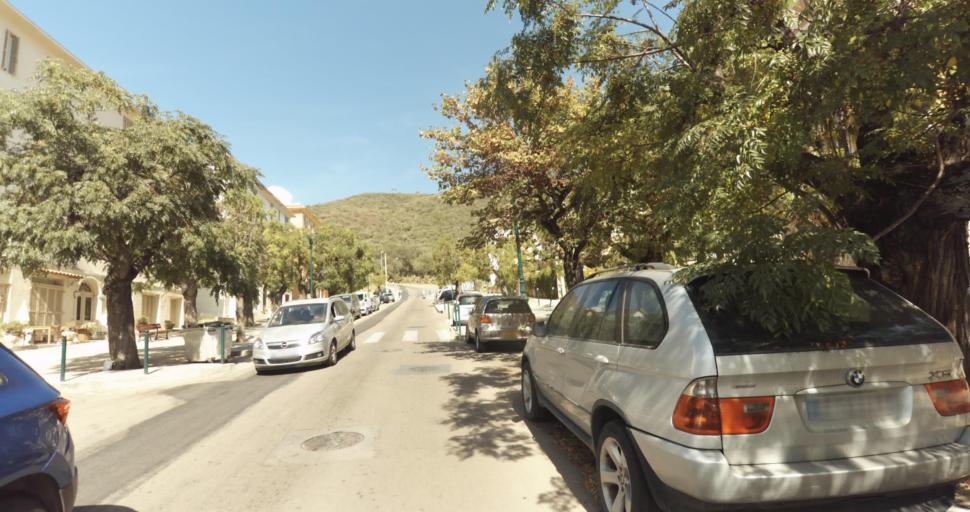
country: FR
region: Corsica
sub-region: Departement de la Corse-du-Sud
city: Ajaccio
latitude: 41.9148
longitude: 8.7246
